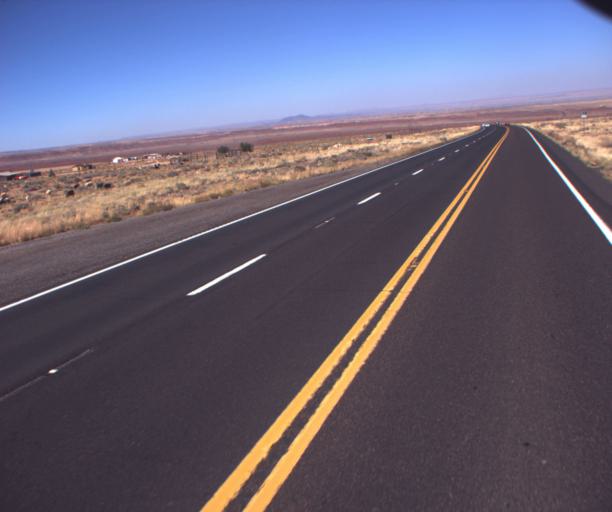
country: US
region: Arizona
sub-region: Coconino County
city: Tuba City
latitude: 35.7573
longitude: -111.4682
